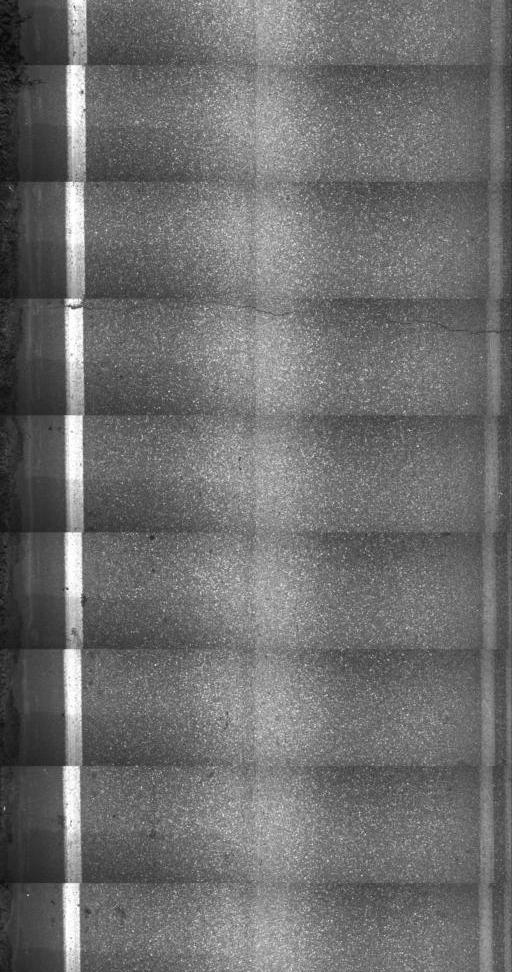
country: US
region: Vermont
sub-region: Chittenden County
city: Williston
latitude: 44.4150
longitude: -72.9989
